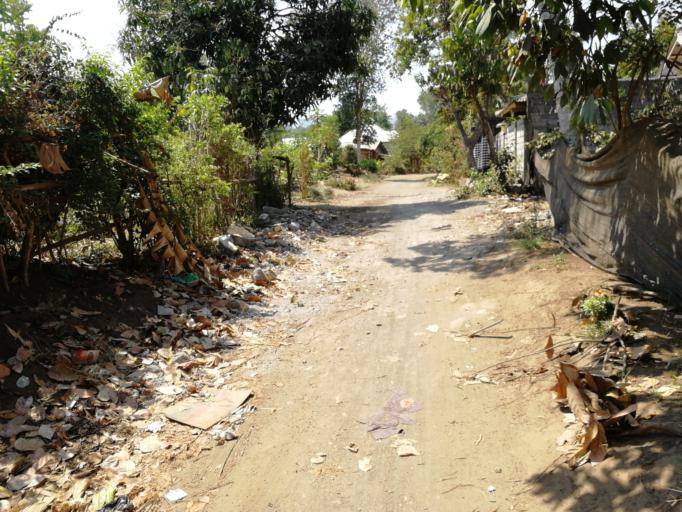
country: ID
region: West Nusa Tenggara
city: Lelongken
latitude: -8.3224
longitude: 116.4904
